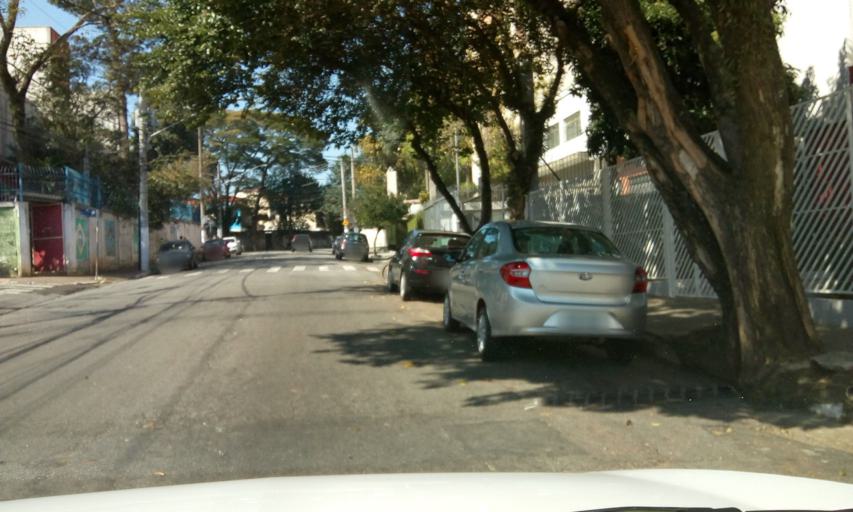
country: BR
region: Sao Paulo
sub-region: Diadema
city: Diadema
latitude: -23.6419
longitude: -46.6684
